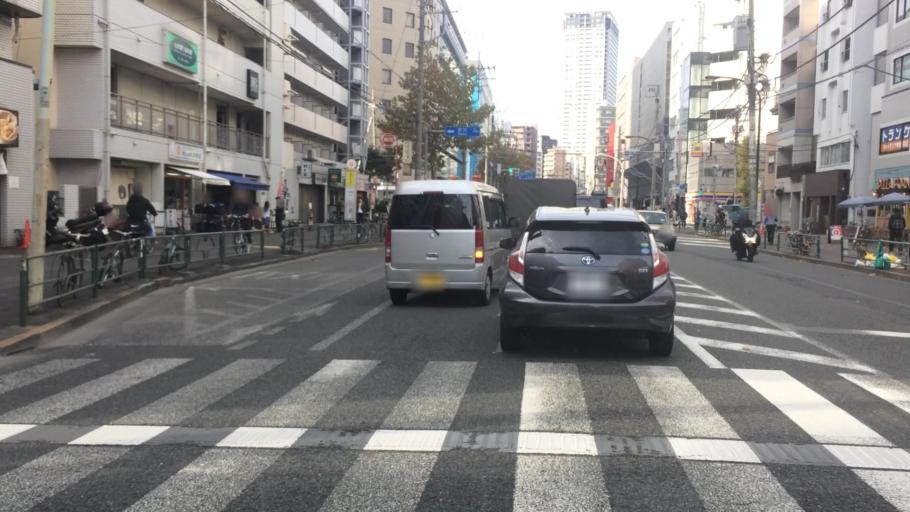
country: JP
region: Tokyo
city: Tokyo
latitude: 35.6473
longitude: 139.6947
